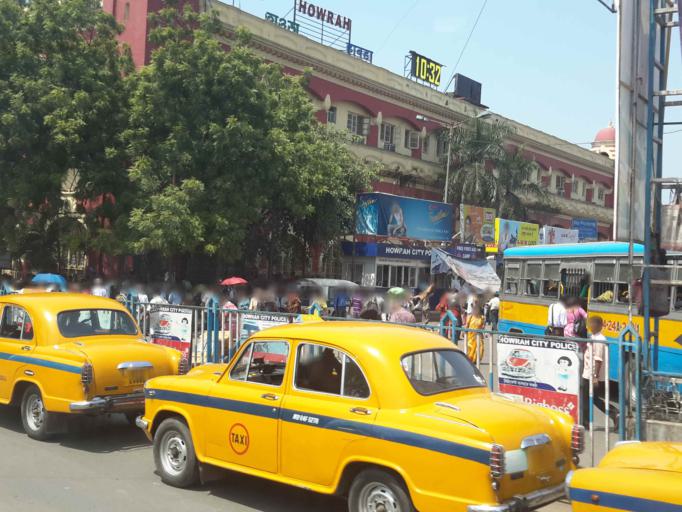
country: IN
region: West Bengal
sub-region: Kolkata
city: Bara Bazar
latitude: 22.5844
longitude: 88.3439
